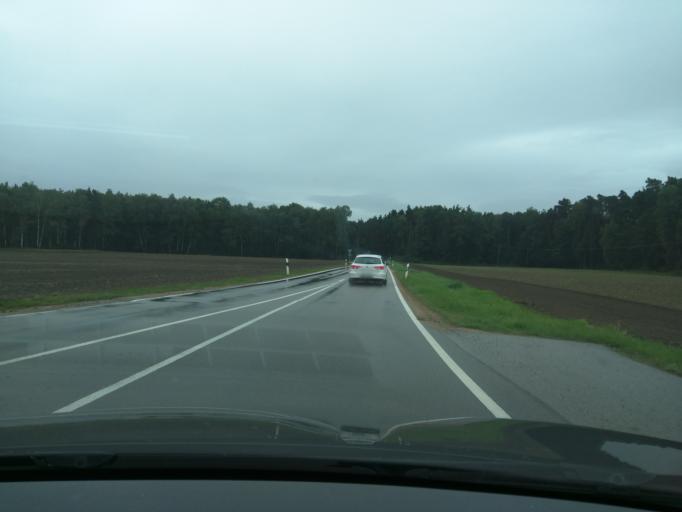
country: DE
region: Bavaria
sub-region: Upper Palatinate
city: Wackersdorf
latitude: 49.3527
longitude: 12.1626
